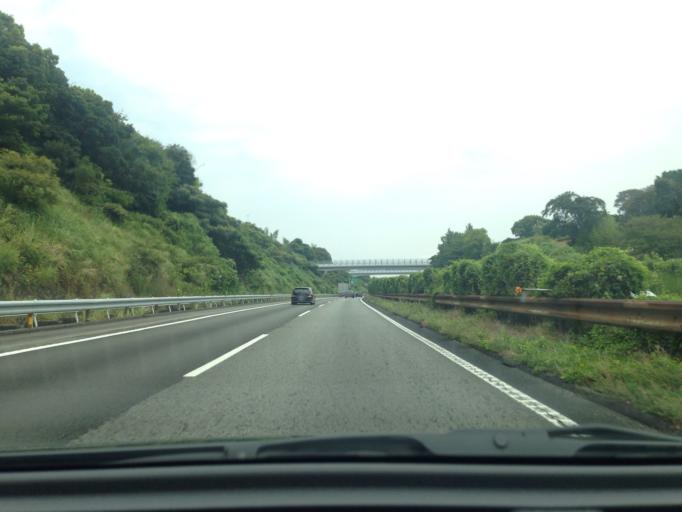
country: JP
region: Shizuoka
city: Shimada
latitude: 34.7822
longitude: 138.2298
